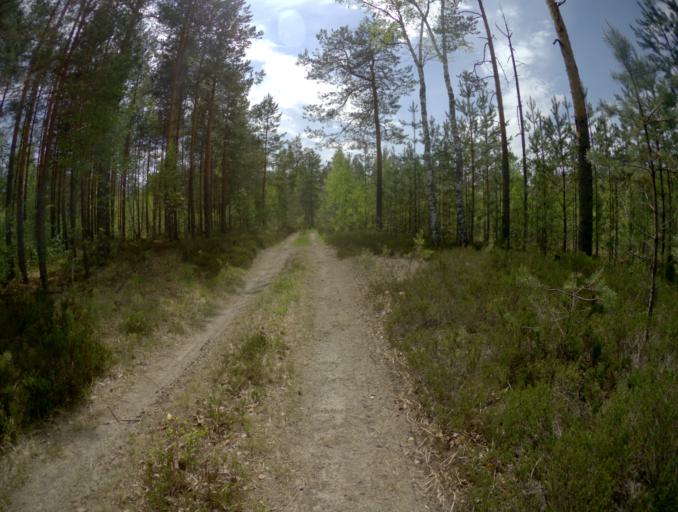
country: RU
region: Vladimir
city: Ivanishchi
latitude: 55.6891
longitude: 40.4050
